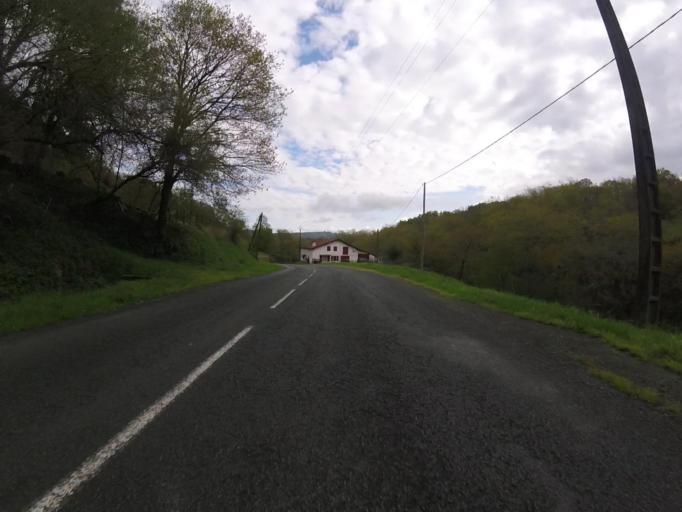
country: FR
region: Aquitaine
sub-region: Departement des Pyrenees-Atlantiques
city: Sare
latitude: 43.2926
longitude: -1.5937
